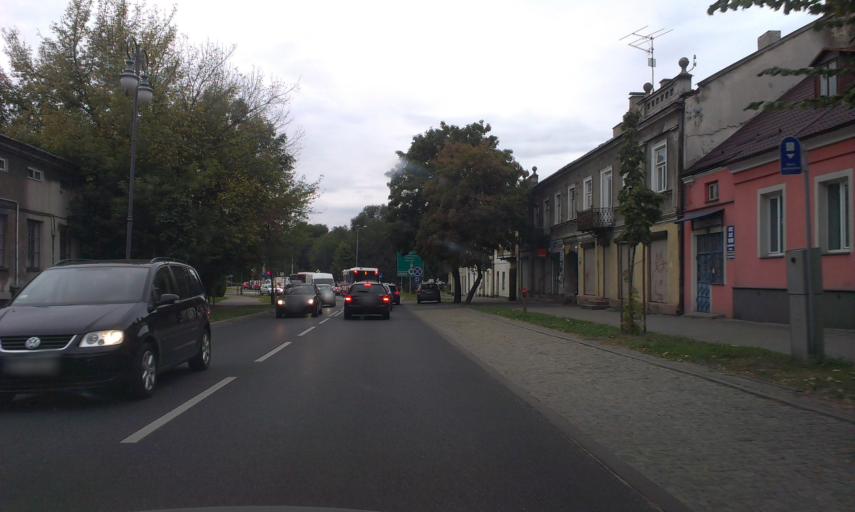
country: PL
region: Masovian Voivodeship
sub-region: Radom
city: Radom
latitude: 51.4043
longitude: 21.1428
